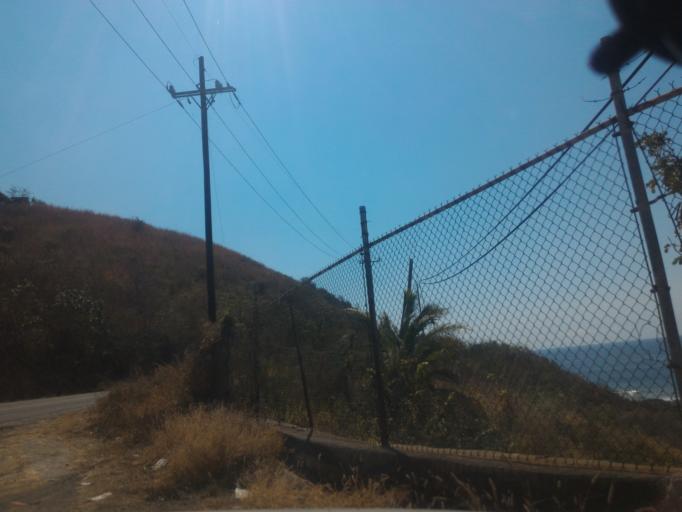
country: MX
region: Michoacan
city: Coahuayana Viejo
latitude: 18.5744
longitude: -103.6623
